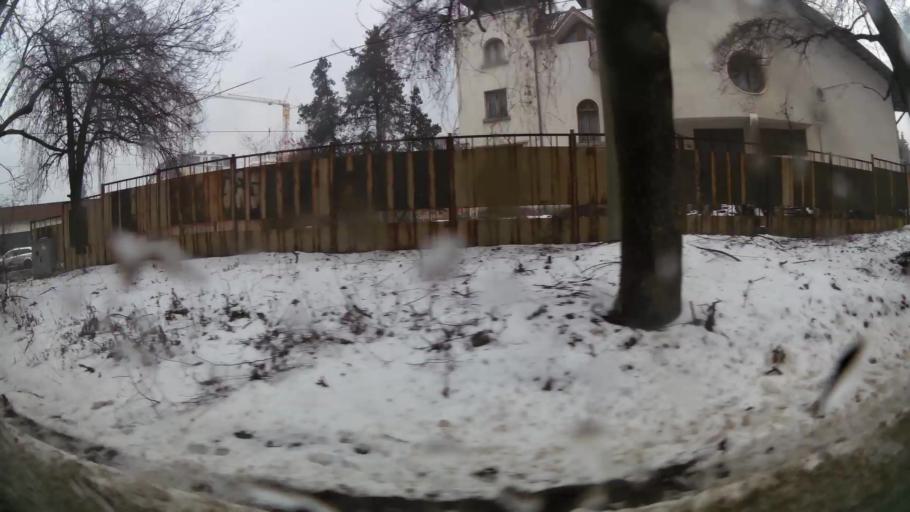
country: BG
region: Sofia-Capital
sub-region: Stolichna Obshtina
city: Sofia
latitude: 42.6778
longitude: 23.2656
